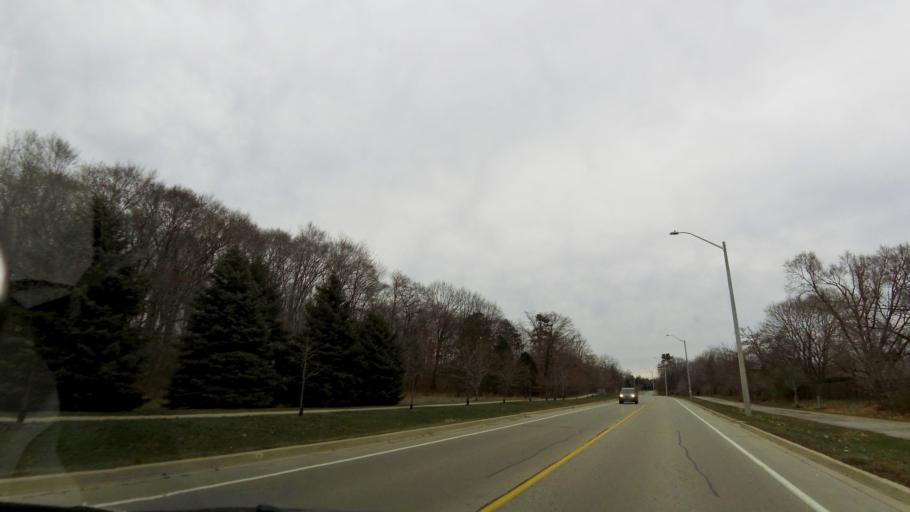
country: CA
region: Ontario
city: Oakville
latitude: 43.4844
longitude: -79.6471
